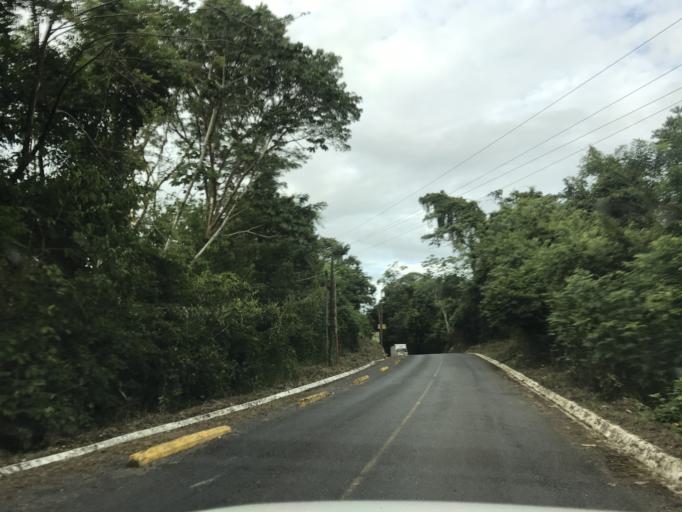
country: GT
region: Izabal
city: Morales
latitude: 15.6420
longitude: -89.0100
